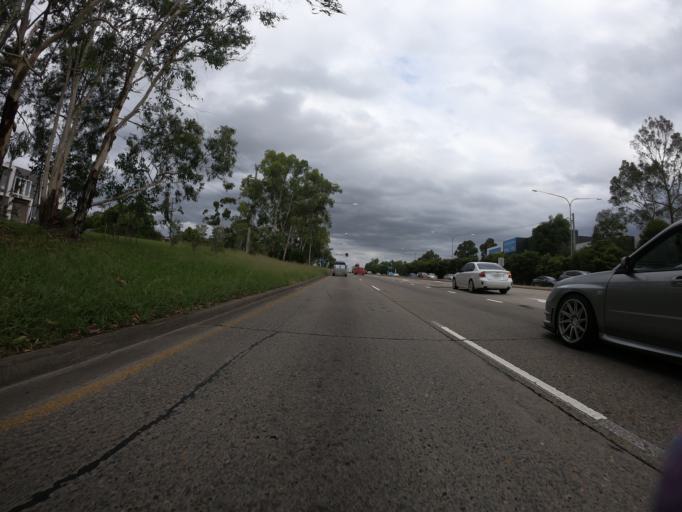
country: AU
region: New South Wales
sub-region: Parramatta
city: Northmead
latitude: -33.7731
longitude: 150.9607
